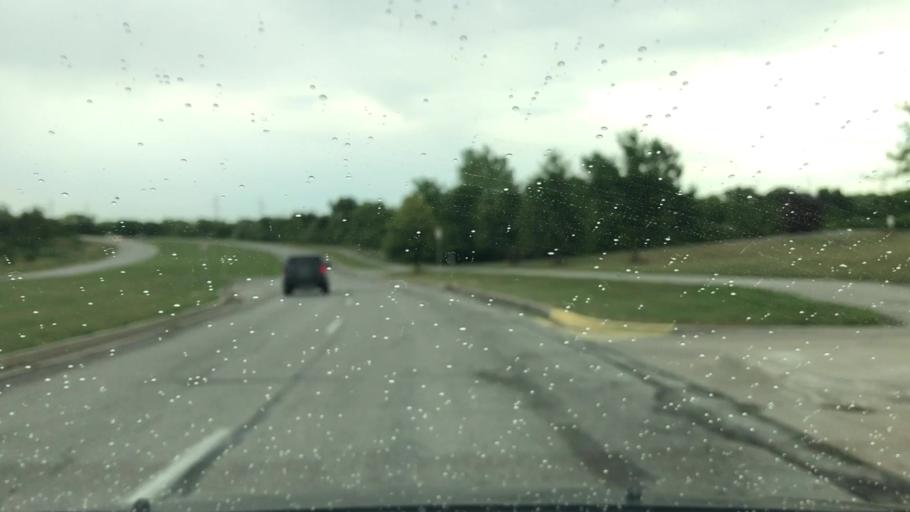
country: US
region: Missouri
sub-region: Jackson County
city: Grandview
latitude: 38.9230
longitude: -94.4850
